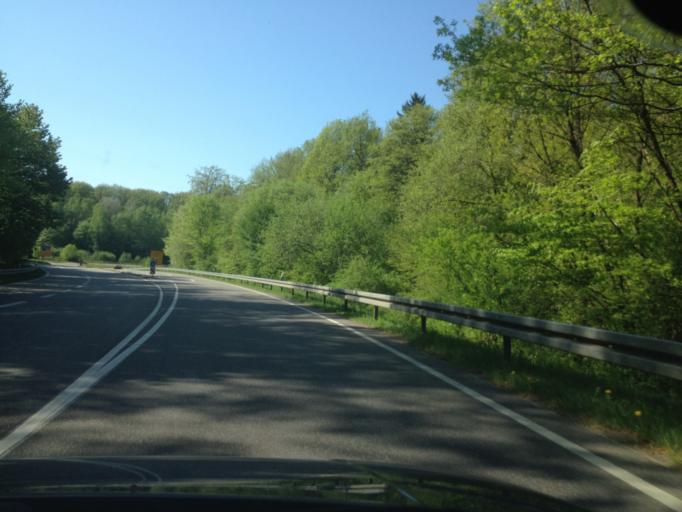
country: DE
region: Saarland
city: Sulzbach
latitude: 49.2748
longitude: 7.0644
